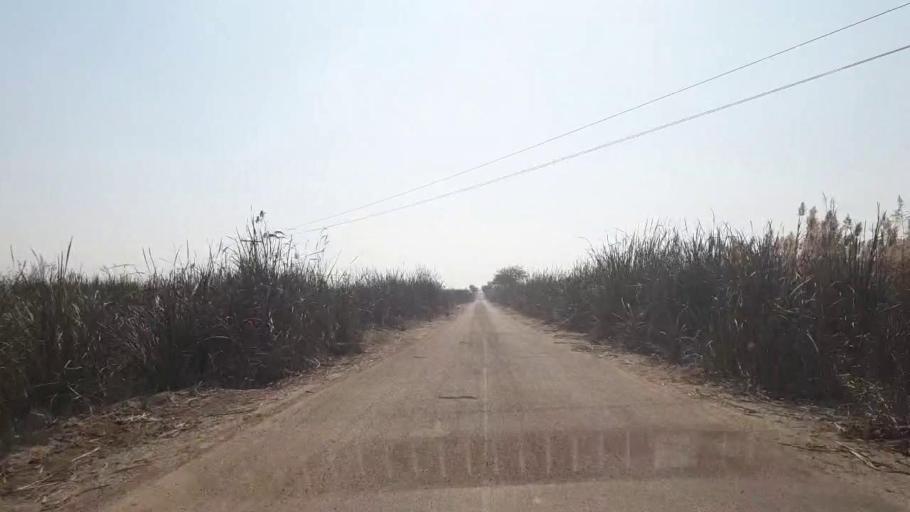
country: PK
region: Sindh
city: Sakrand
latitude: 26.0271
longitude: 68.4382
